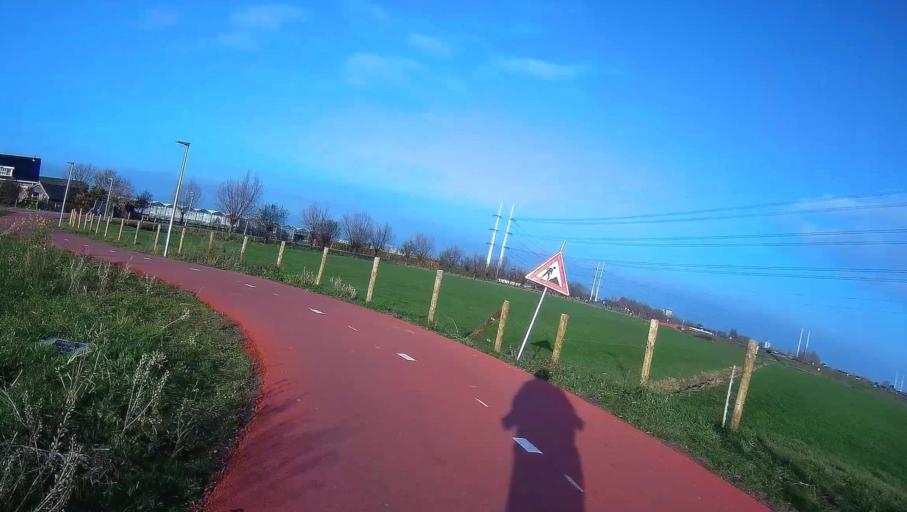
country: NL
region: South Holland
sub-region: Gemeente Lansingerland
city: Berkel en Rodenrijs
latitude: 52.0256
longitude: 4.4682
